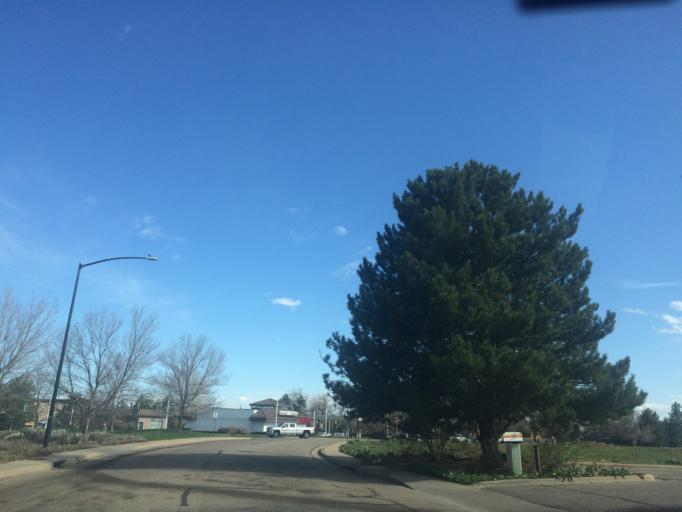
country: US
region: Colorado
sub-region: Boulder County
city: Lafayette
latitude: 40.0018
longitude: -105.1056
